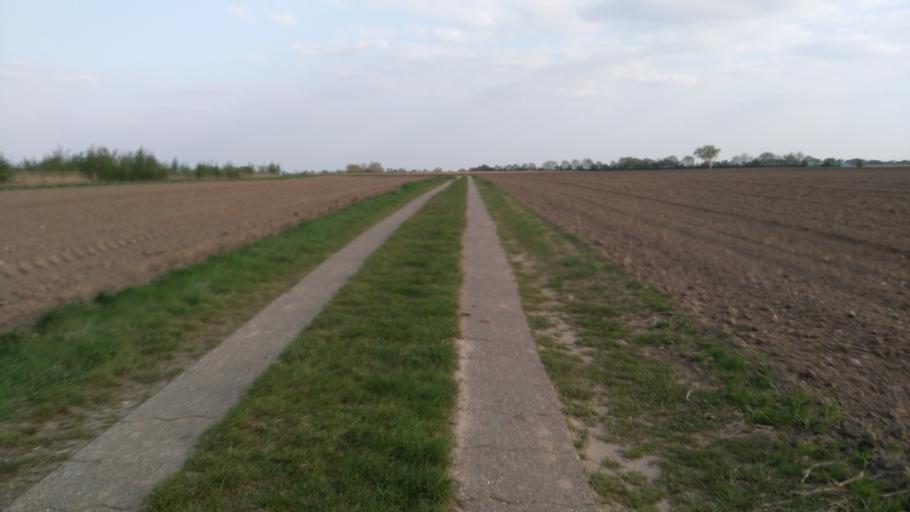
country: DE
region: Lower Saxony
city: Apensen
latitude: 53.4632
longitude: 9.6422
